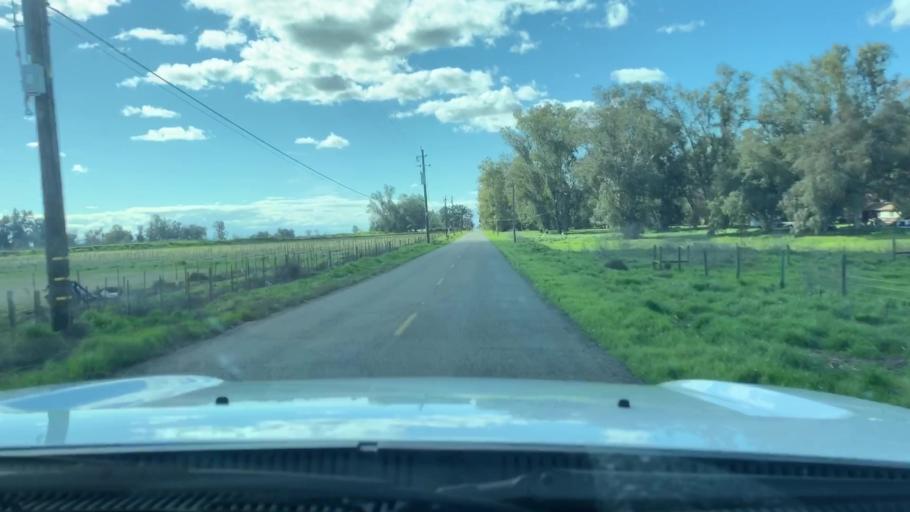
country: US
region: California
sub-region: Fresno County
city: Fowler
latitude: 36.5617
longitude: -119.7032
